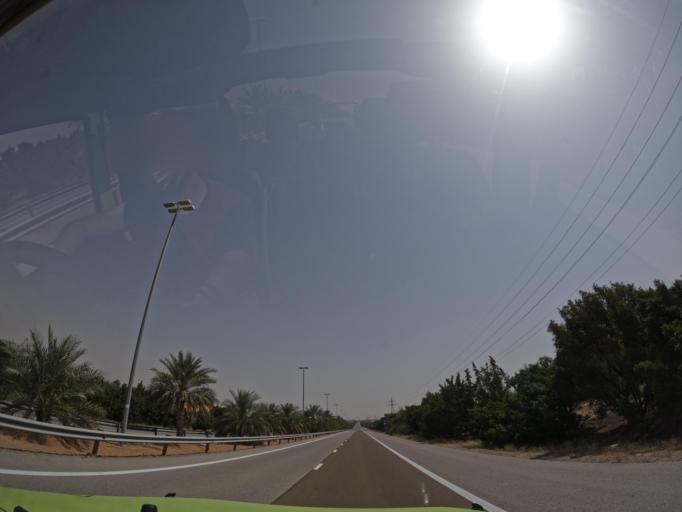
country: OM
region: Al Buraimi
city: Al Buraymi
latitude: 24.7211
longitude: 55.7709
